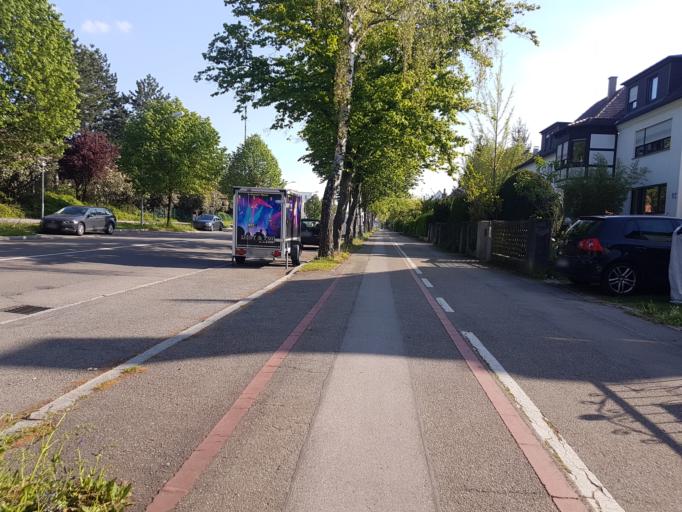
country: DE
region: Baden-Wuerttemberg
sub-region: Regierungsbezirk Stuttgart
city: Kornwestheim
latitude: 48.8586
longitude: 9.1853
